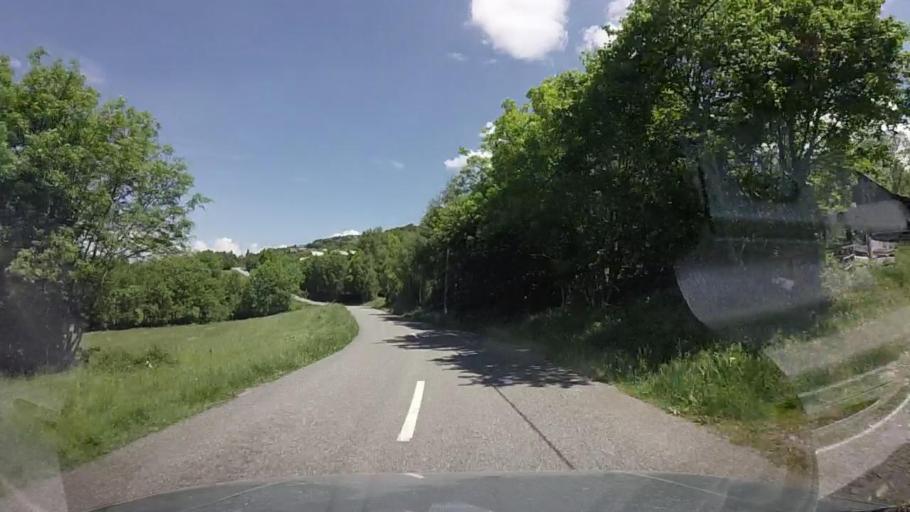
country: FR
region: Provence-Alpes-Cote d'Azur
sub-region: Departement des Alpes-de-Haute-Provence
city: Seyne-les-Alpes
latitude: 44.3881
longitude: 6.3478
